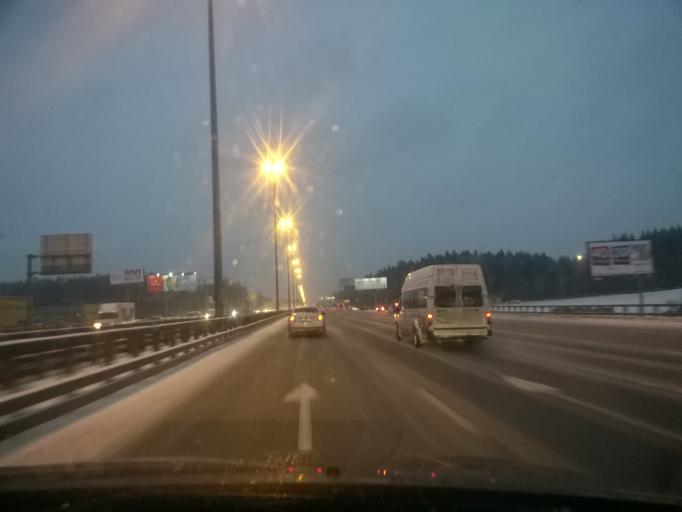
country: RU
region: Moskovskaya
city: Moskovskiy
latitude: 55.6089
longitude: 37.3540
